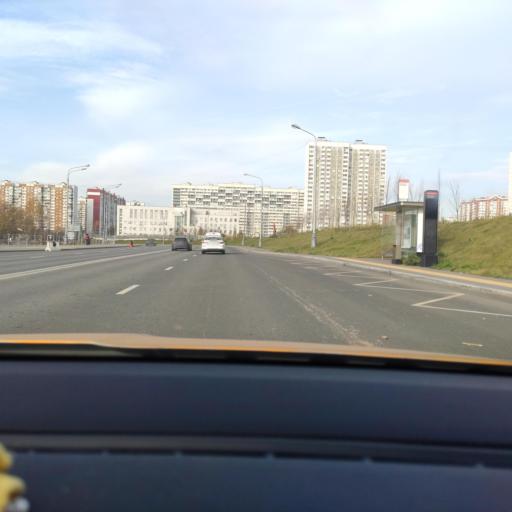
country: RU
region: Moscow
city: Ramenki
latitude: 55.6933
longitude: 37.5129
